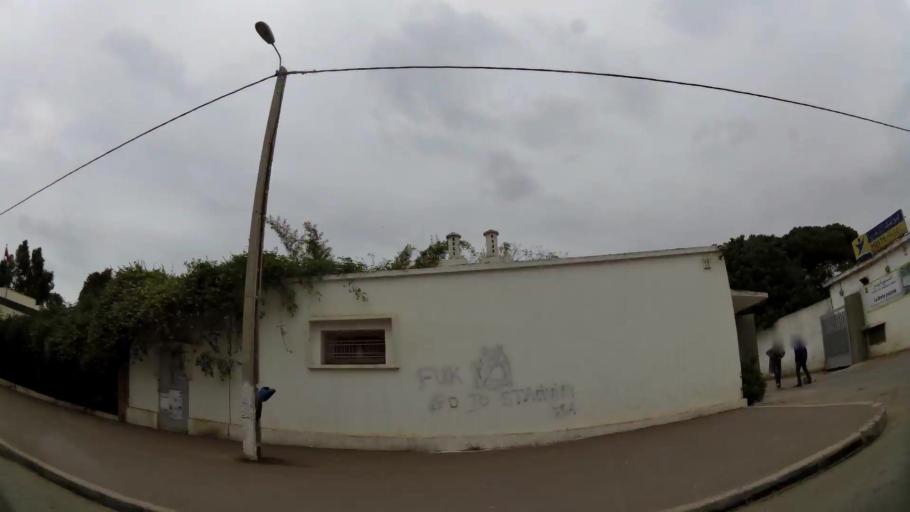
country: MA
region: Rabat-Sale-Zemmour-Zaer
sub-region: Rabat
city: Rabat
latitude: 33.9756
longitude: -6.8188
